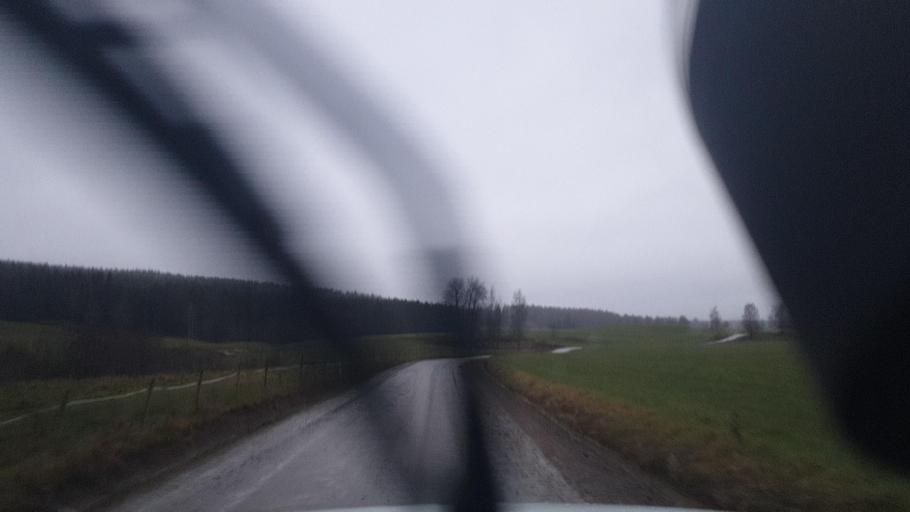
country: SE
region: Vaermland
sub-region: Eda Kommun
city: Amotfors
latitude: 59.7185
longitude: 12.1462
